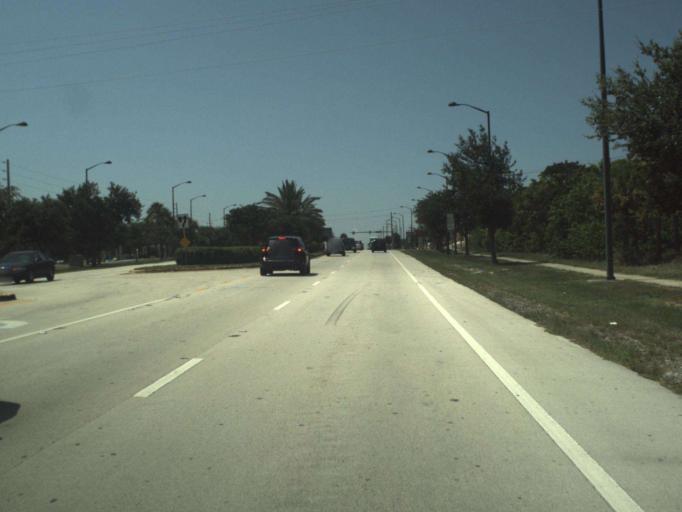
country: US
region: Florida
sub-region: Saint Lucie County
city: Fort Pierce
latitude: 27.4676
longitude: -80.3323
